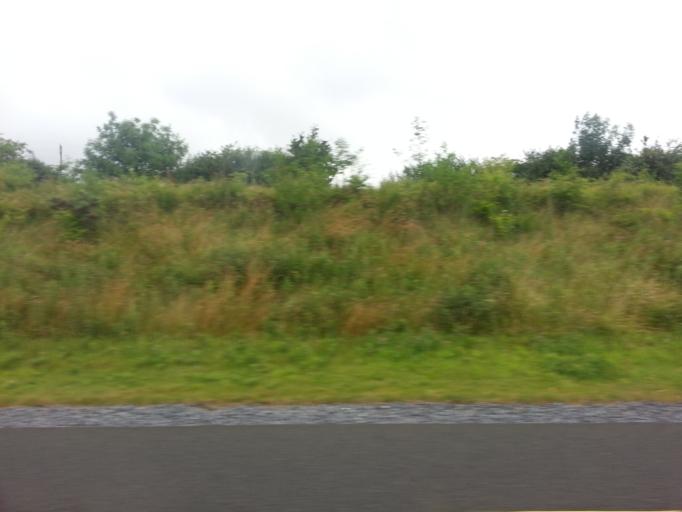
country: IE
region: Leinster
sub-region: Kilkenny
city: Kilkenny
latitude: 52.6537
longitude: -7.1983
